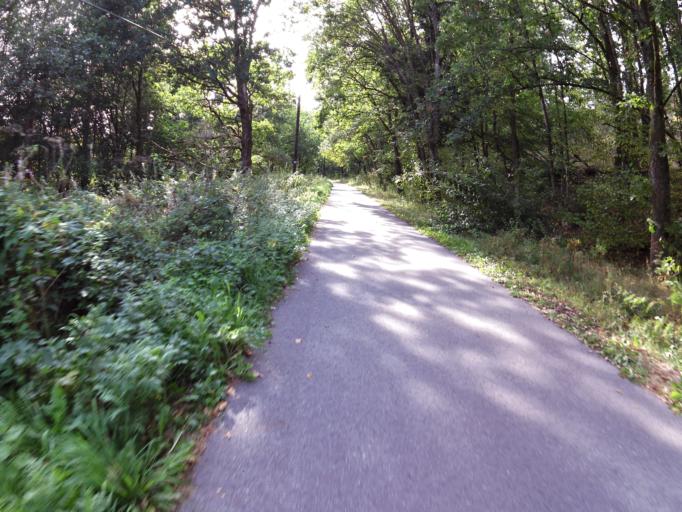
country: DE
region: Rheinland-Pfalz
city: Winterspelt
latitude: 50.2365
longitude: 6.1780
